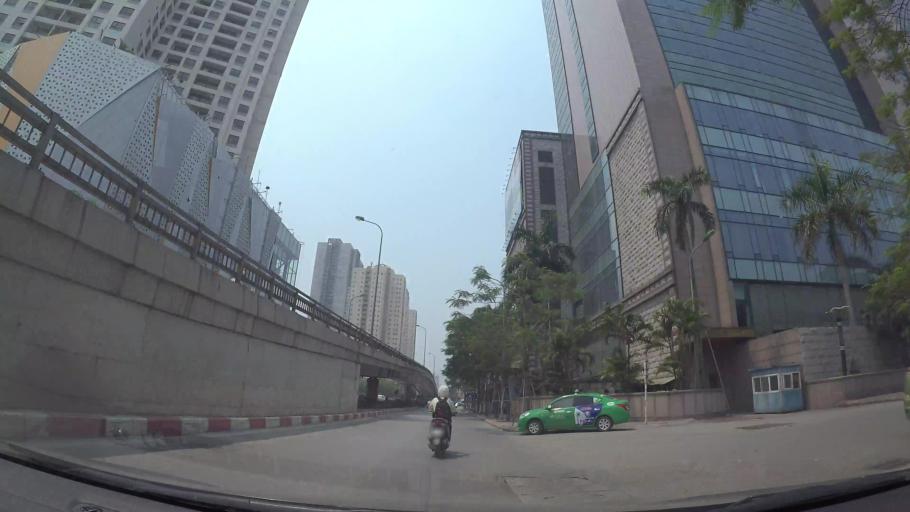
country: VN
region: Ha Noi
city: Thanh Xuan
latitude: 21.0068
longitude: 105.7966
